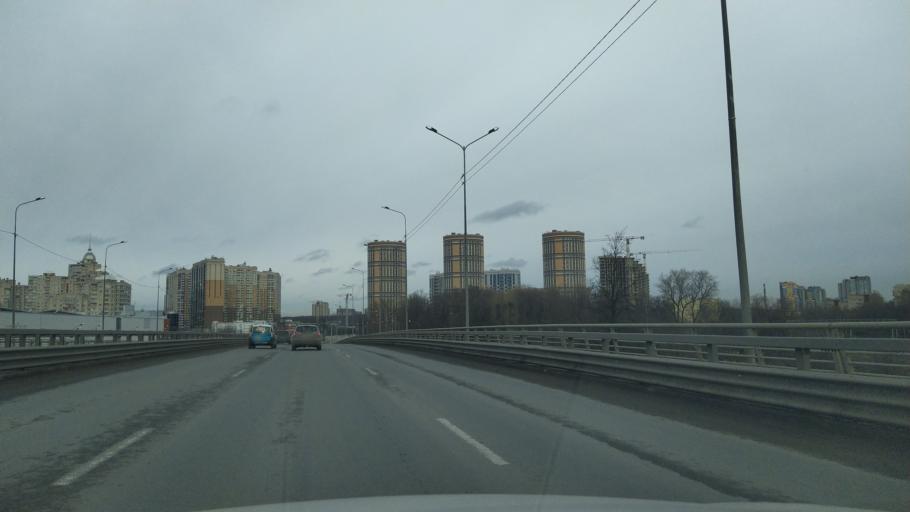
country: RU
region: Leningrad
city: Chernaya Rechka
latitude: 59.9929
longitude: 30.2993
